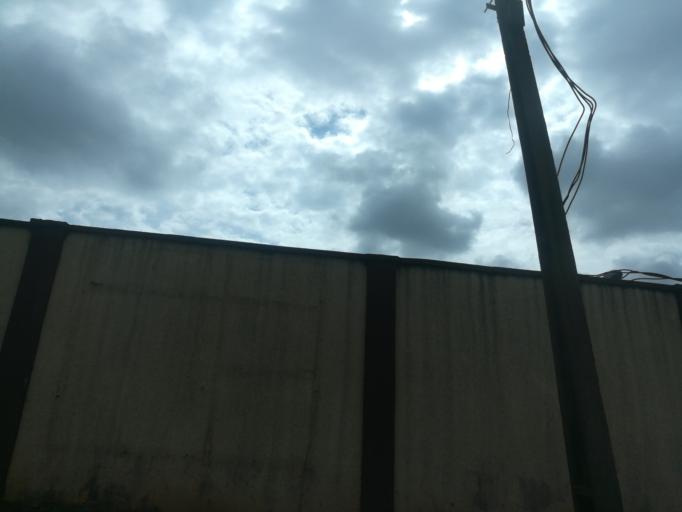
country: NG
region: Lagos
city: Agege
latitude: 6.6243
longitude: 3.3308
